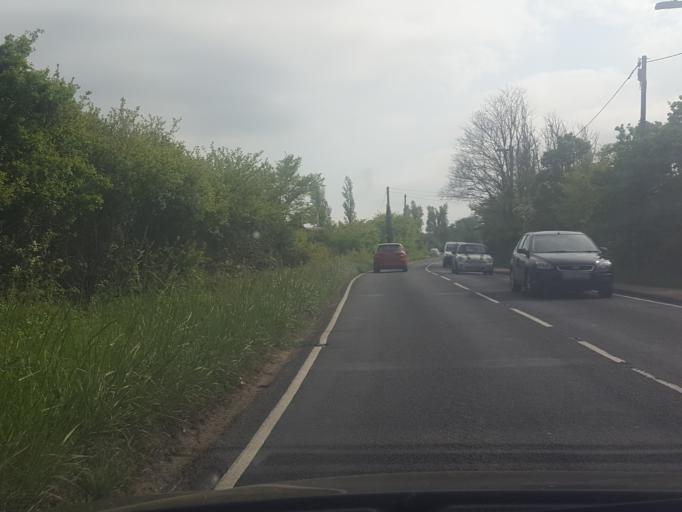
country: GB
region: England
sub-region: Essex
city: Frinton-on-Sea
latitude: 51.8382
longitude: 1.2155
